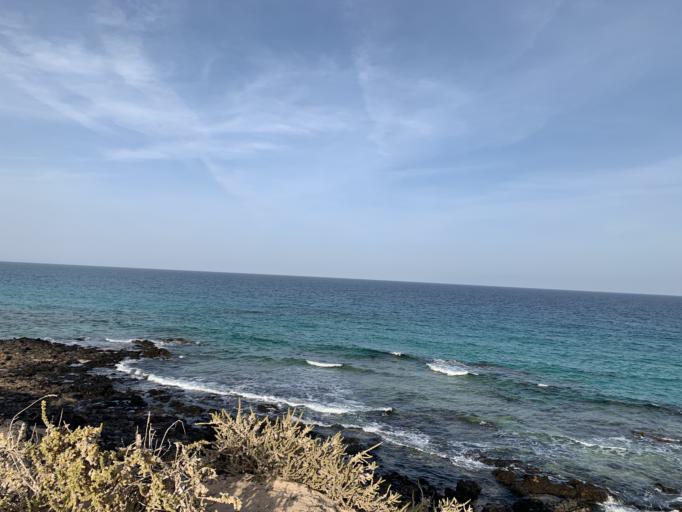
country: ES
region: Canary Islands
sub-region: Provincia de Las Palmas
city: Corralejo
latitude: 28.6716
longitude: -13.8330
